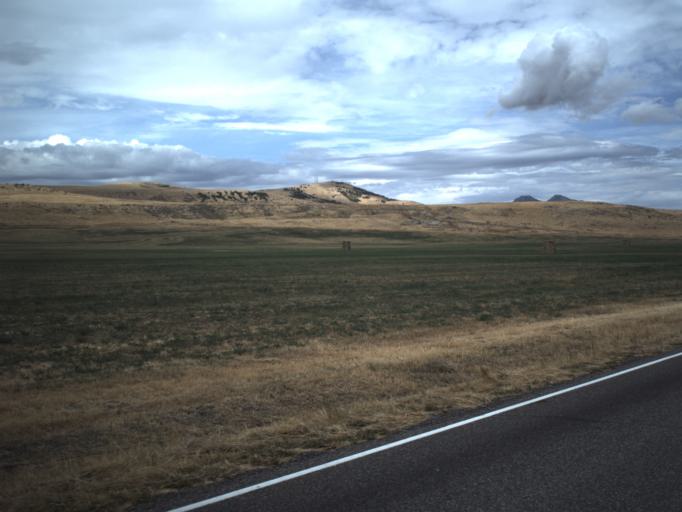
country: US
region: Utah
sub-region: Cache County
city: Benson
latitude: 41.8011
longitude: -111.9920
